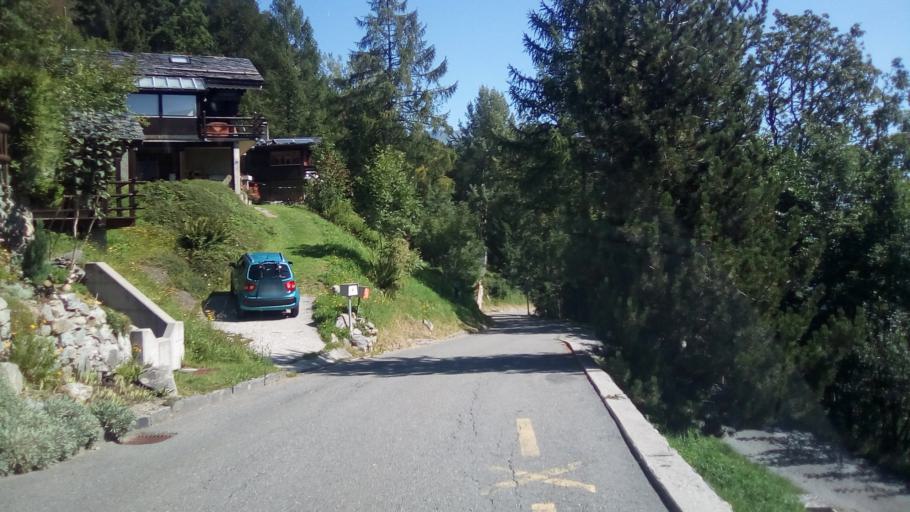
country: CH
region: Valais
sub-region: Saint-Maurice District
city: Salvan
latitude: 46.1105
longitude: 7.0037
